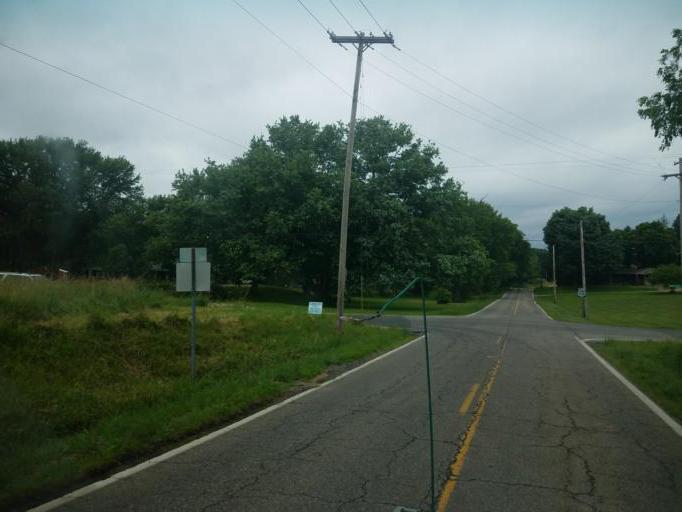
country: US
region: Ohio
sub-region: Columbiana County
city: Columbiana
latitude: 40.8331
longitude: -80.7075
